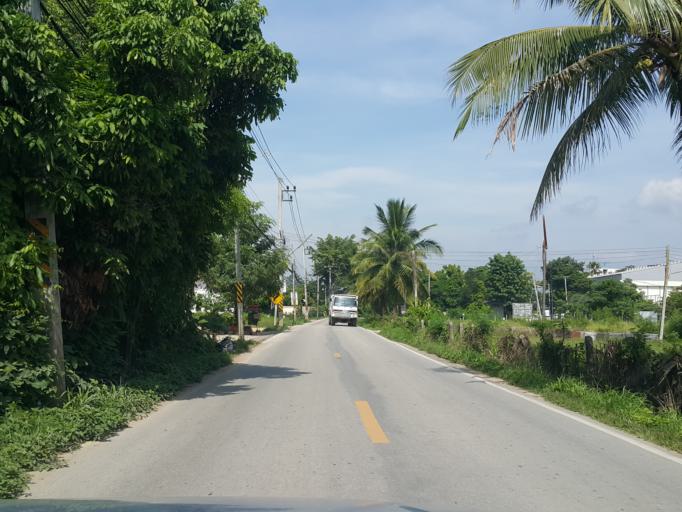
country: TH
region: Chiang Mai
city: Saraphi
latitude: 18.6918
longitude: 99.0538
